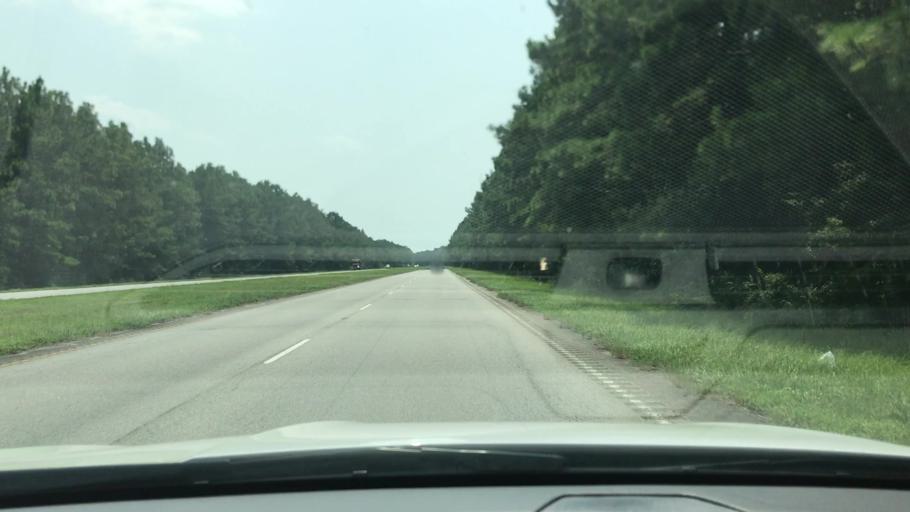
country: US
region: South Carolina
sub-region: Charleston County
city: Awendaw
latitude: 32.9783
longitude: -79.6648
